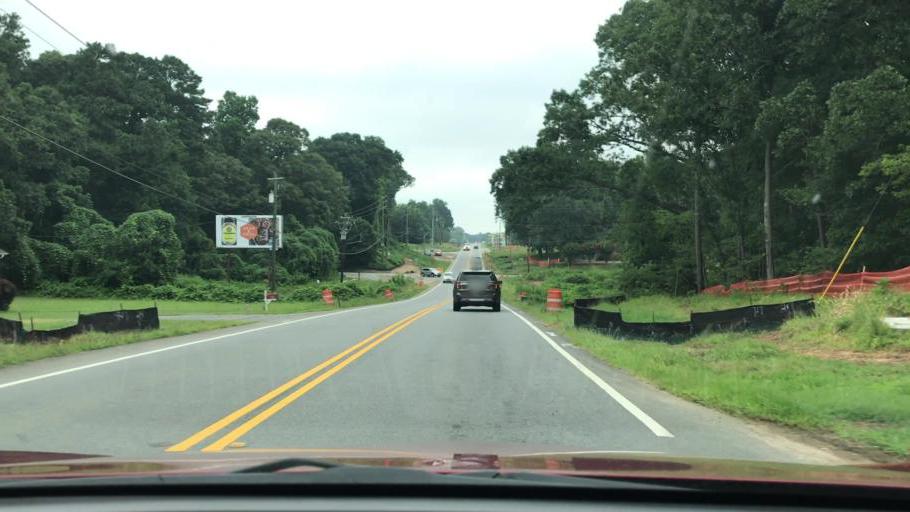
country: US
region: Georgia
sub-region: Gwinnett County
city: Suwanee
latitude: 34.0487
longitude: -84.0735
